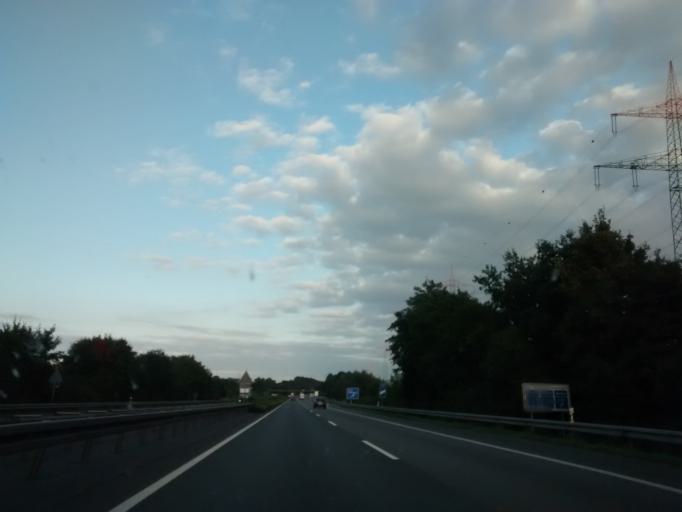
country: DE
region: North Rhine-Westphalia
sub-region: Regierungsbezirk Munster
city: Lotte
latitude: 52.2646
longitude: 7.8844
